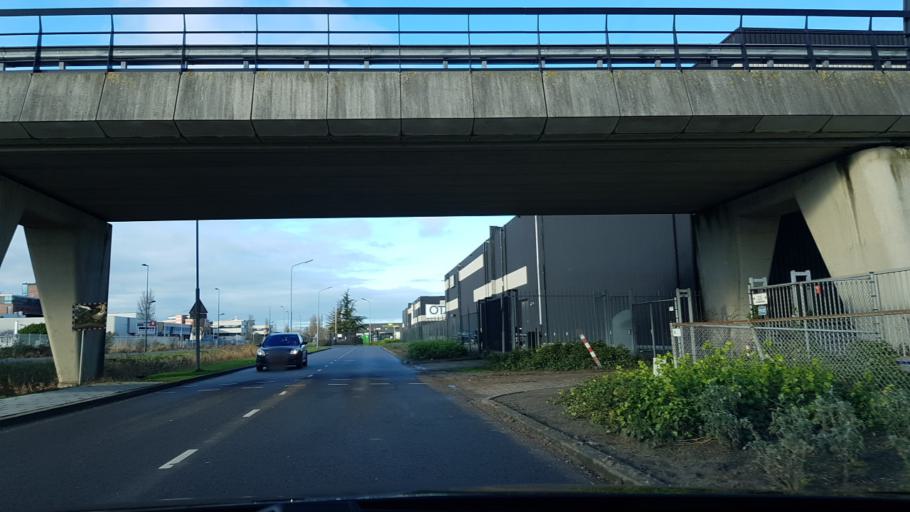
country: NL
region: North Holland
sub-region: Gemeente Haarlemmermeer
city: Hoofddorp
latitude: 52.2920
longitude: 4.7236
